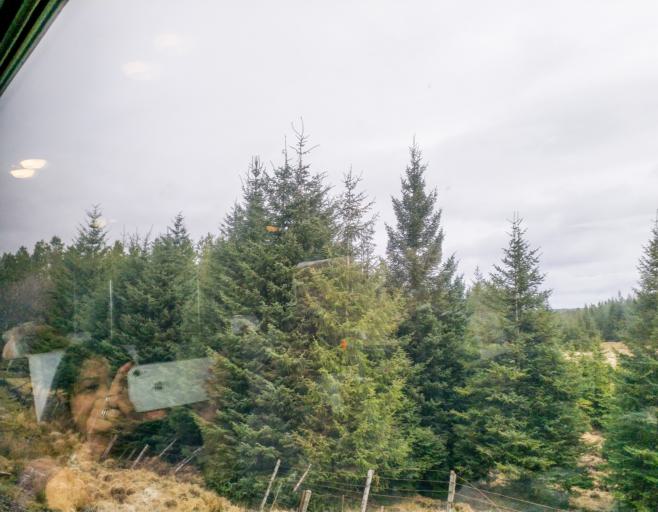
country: GB
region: Scotland
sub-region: Highland
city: Spean Bridge
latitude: 56.6510
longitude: -4.5670
